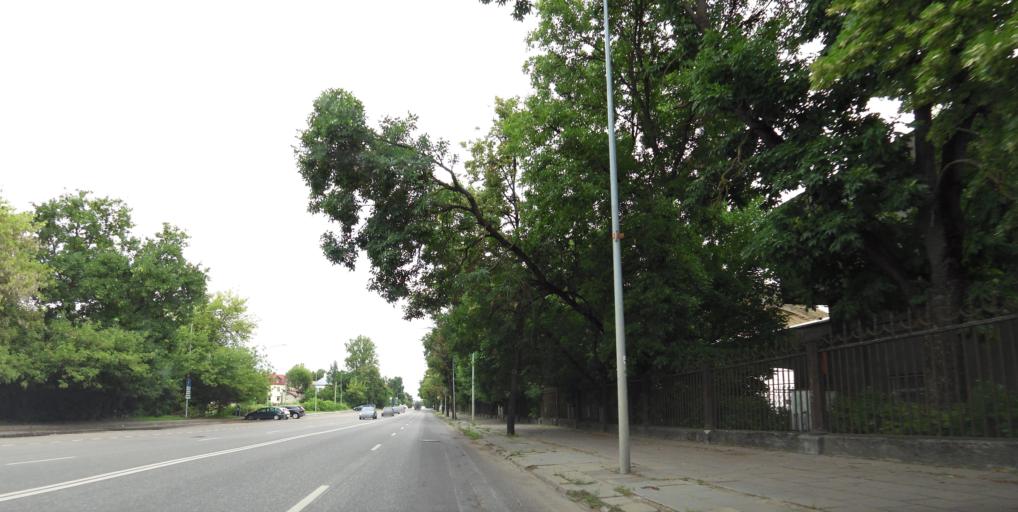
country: LT
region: Vilnius County
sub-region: Vilnius
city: Vilnius
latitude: 54.6927
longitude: 25.2891
